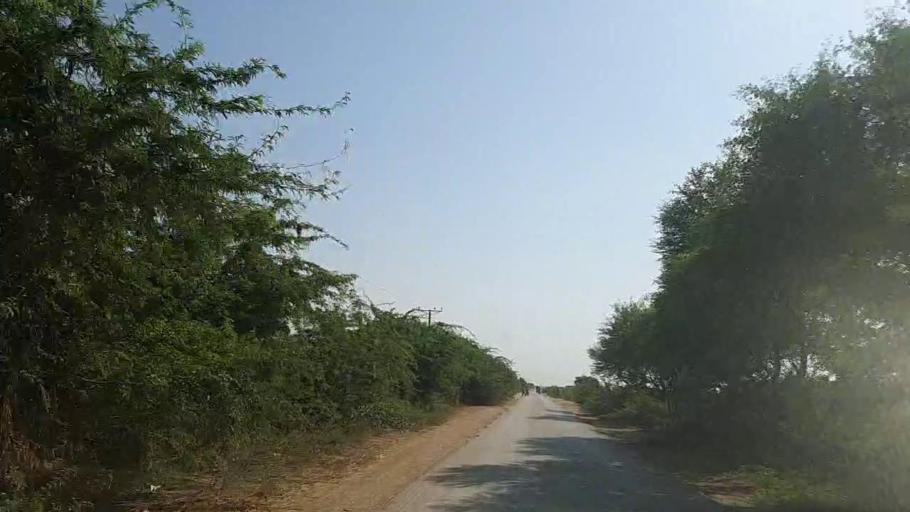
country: PK
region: Sindh
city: Mirpur Batoro
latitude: 24.6384
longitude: 68.2913
